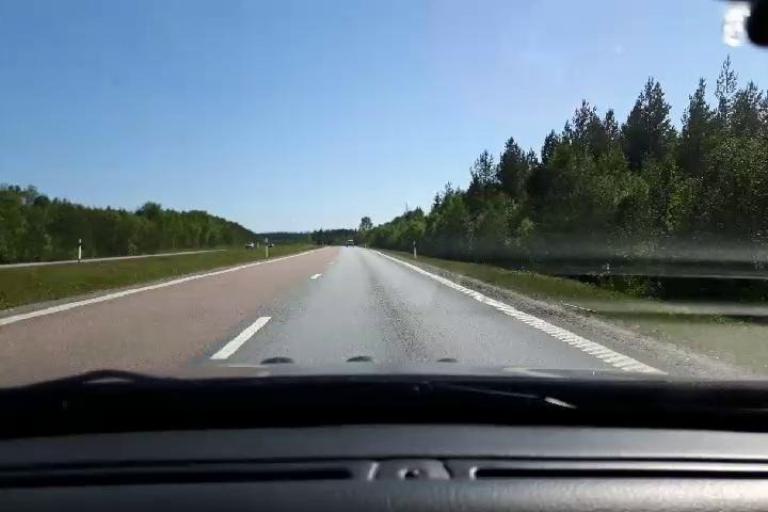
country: SE
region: Gaevleborg
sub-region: Hudiksvalls Kommun
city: Iggesund
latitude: 61.4938
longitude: 16.9839
